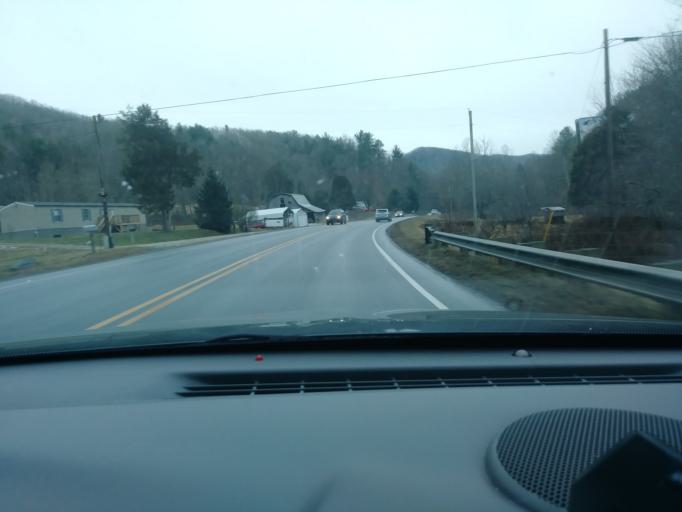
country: US
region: North Carolina
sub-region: Watauga County
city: Foscoe
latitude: 36.2012
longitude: -81.7363
